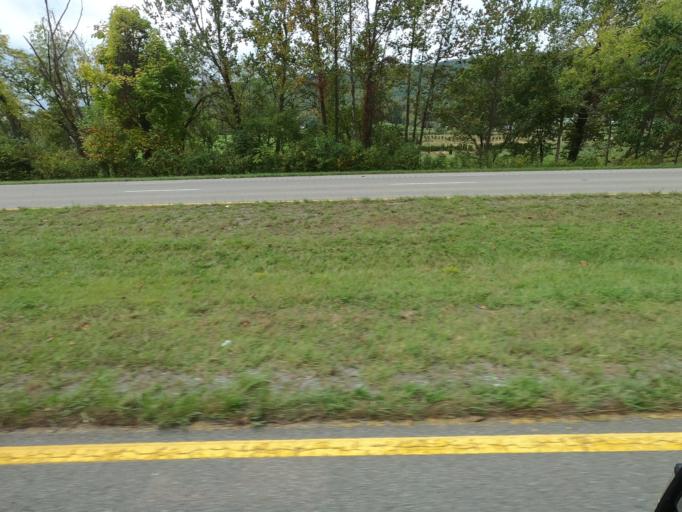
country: US
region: Tennessee
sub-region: Carter County
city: Elizabethton
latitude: 36.2649
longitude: -82.1831
